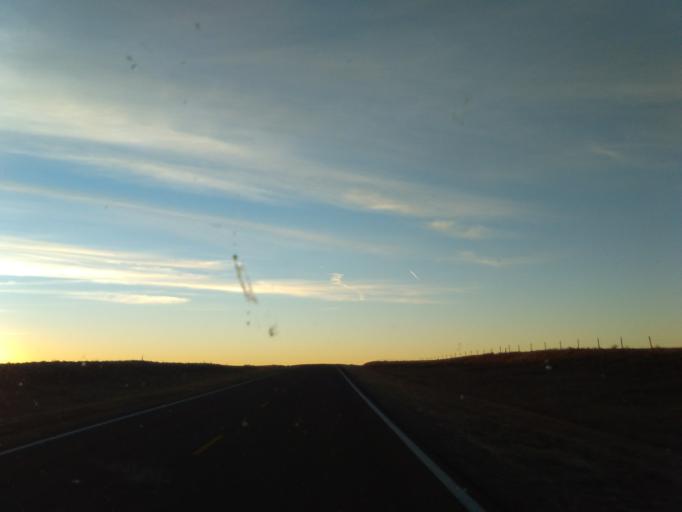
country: US
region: Kansas
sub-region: Wallace County
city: Sharon Springs
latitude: 38.9013
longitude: -101.8160
